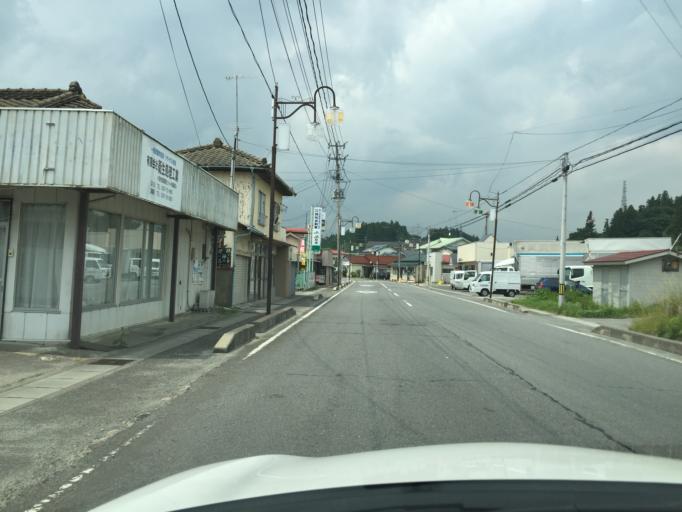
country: JP
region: Fukushima
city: Funehikimachi-funehiki
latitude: 37.2758
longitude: 140.6359
